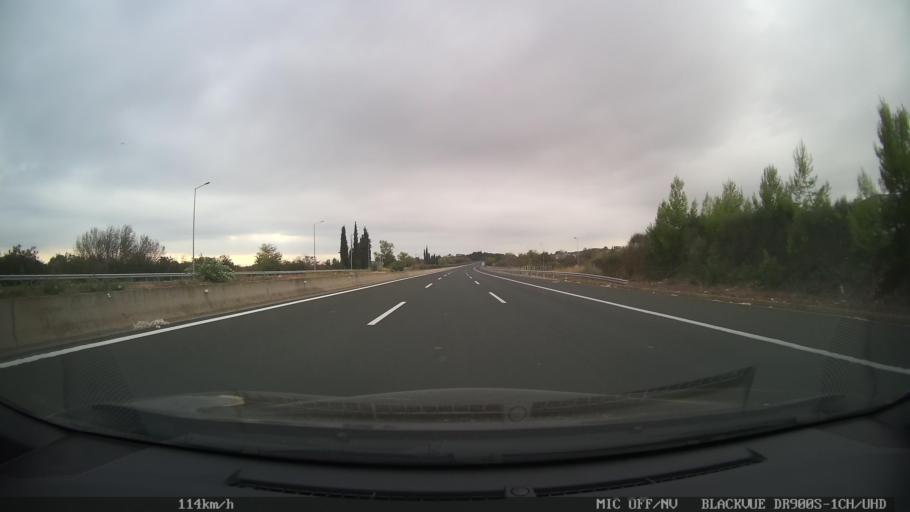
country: GR
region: Central Macedonia
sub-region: Nomos Pierias
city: Makrygialos
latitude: 40.3901
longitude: 22.6047
